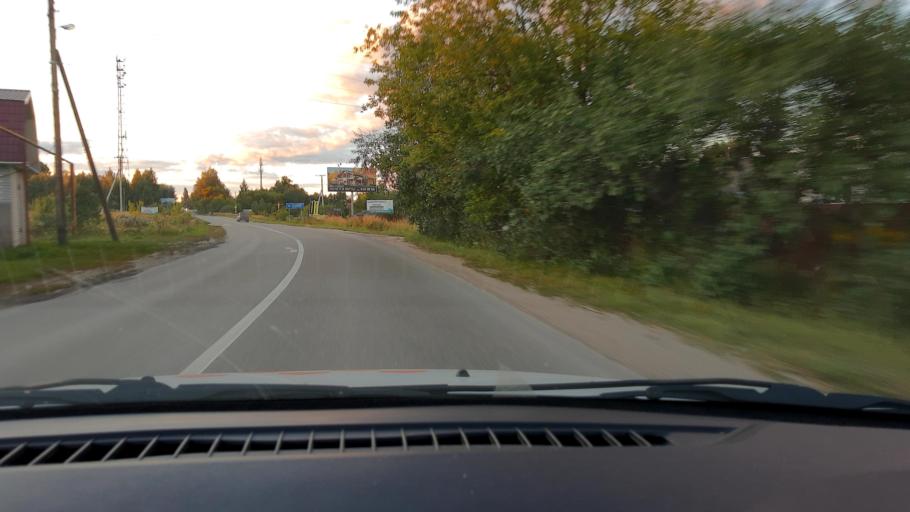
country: RU
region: Nizjnij Novgorod
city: Zavolzh'ye
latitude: 56.7114
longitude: 43.4162
